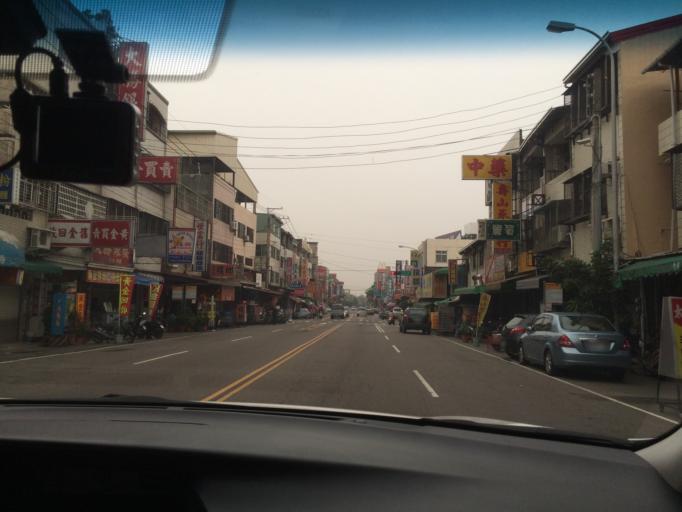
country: TW
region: Taiwan
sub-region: Taichung City
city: Taichung
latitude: 24.1775
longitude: 120.7193
